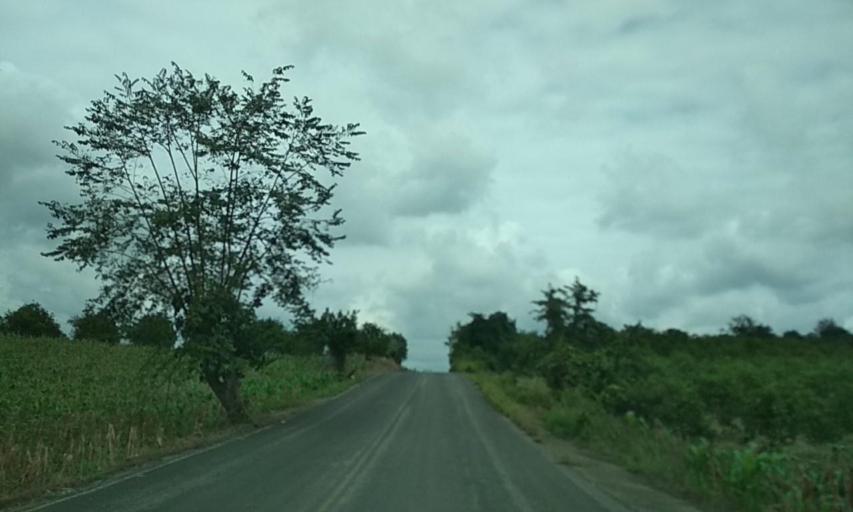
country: MX
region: Veracruz
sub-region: Papantla
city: El Chote
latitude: 20.3516
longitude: -97.3742
